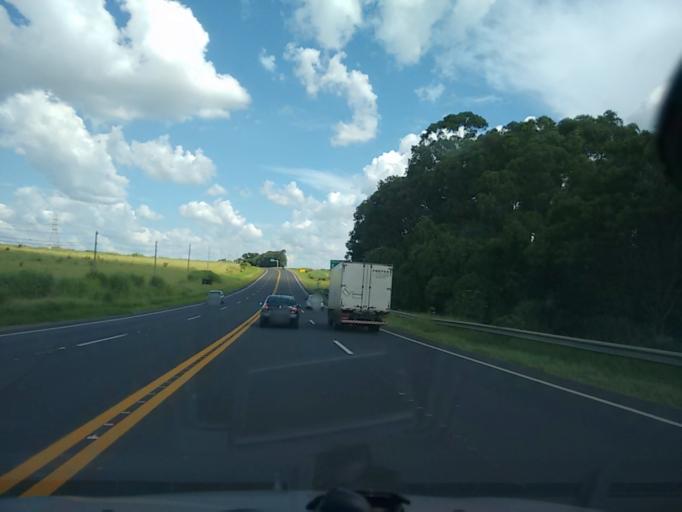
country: BR
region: Sao Paulo
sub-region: Marilia
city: Marilia
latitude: -22.1730
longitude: -49.9819
